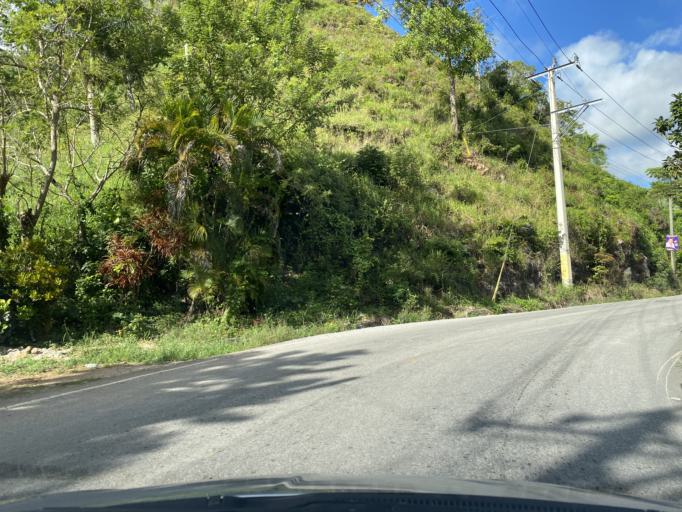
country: DO
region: Samana
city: Las Terrenas
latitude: 19.2670
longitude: -69.5660
